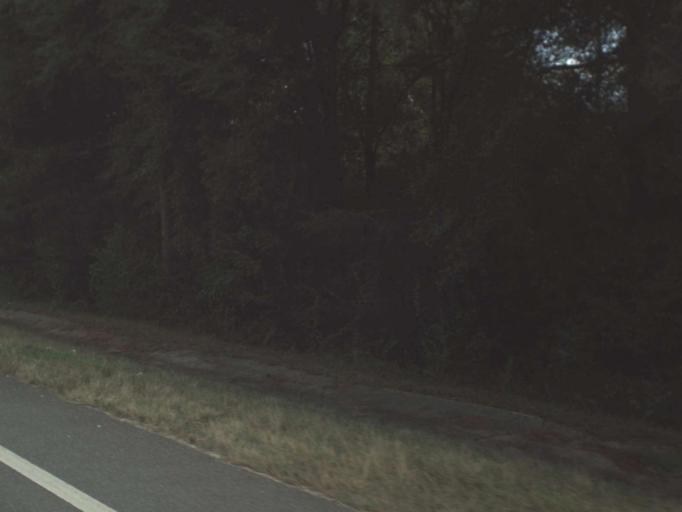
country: US
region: Florida
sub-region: Walton County
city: DeFuniak Springs
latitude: 30.7477
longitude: -86.1144
